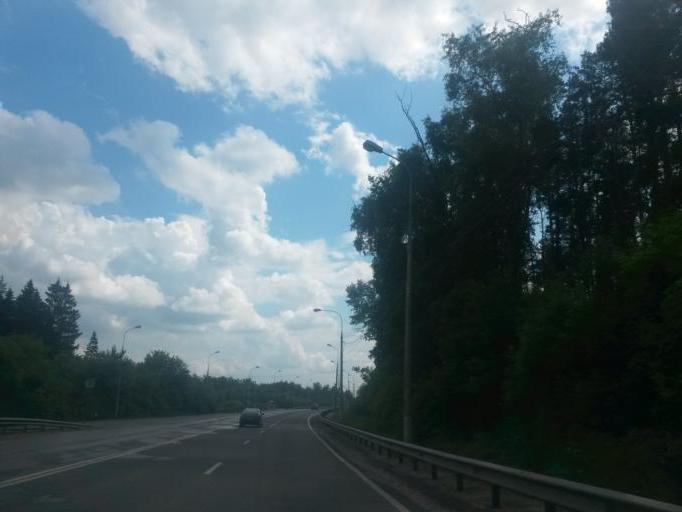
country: RU
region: Moskovskaya
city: Vostryakovo
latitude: 55.4021
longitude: 37.7862
